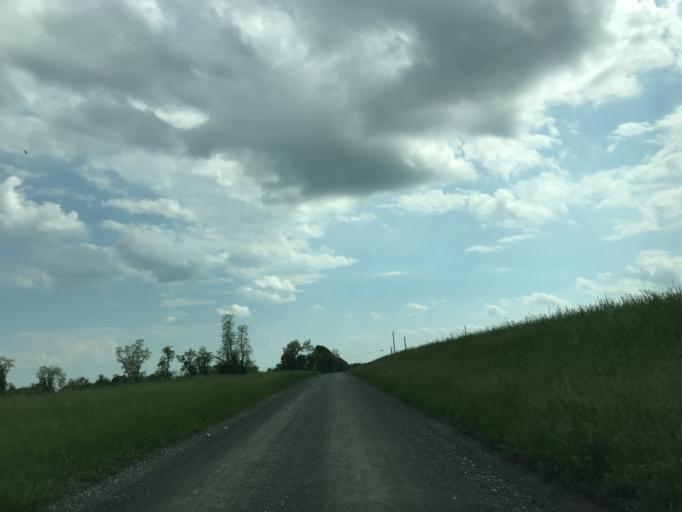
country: US
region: Pennsylvania
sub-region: York County
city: Susquehanna Trails
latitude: 39.7011
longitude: -76.3428
